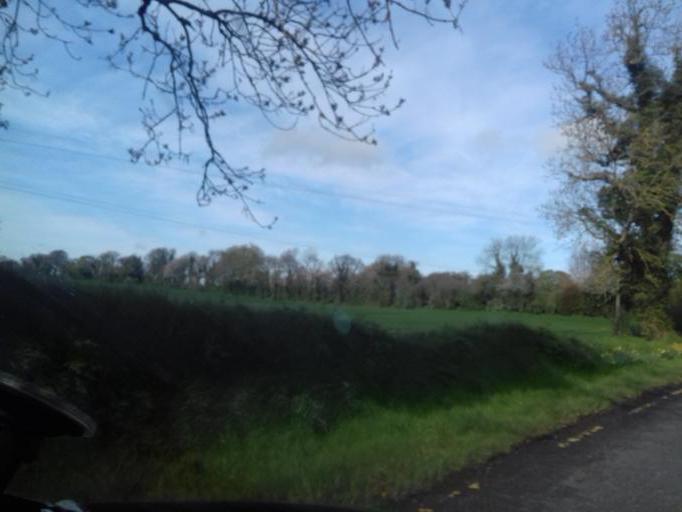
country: IE
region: Leinster
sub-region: An Mhi
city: Kells
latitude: 53.7240
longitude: -6.8617
